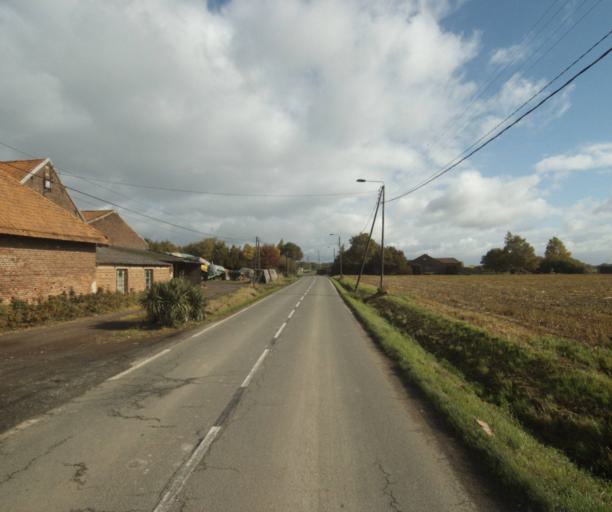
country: FR
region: Nord-Pas-de-Calais
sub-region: Departement du Nord
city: Verlinghem
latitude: 50.6871
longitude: 3.0074
